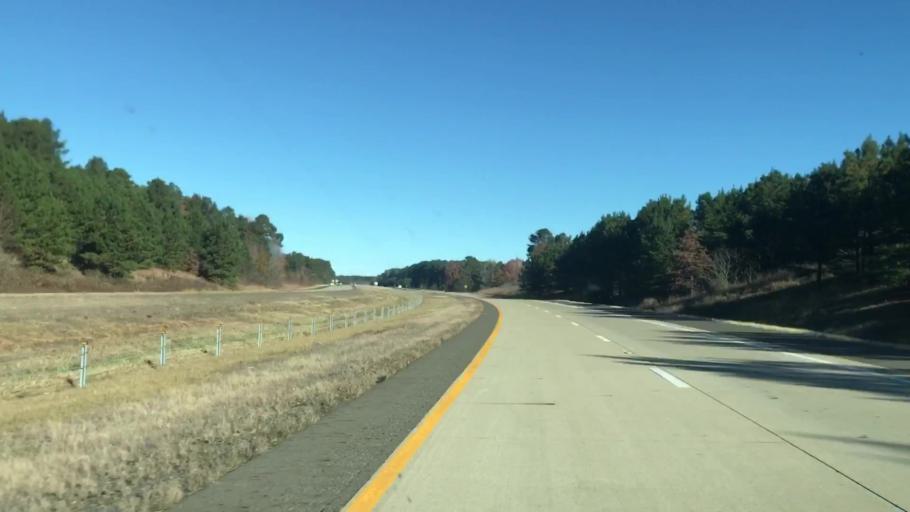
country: US
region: Louisiana
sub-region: Caddo Parish
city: Vivian
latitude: 33.0879
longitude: -93.8947
